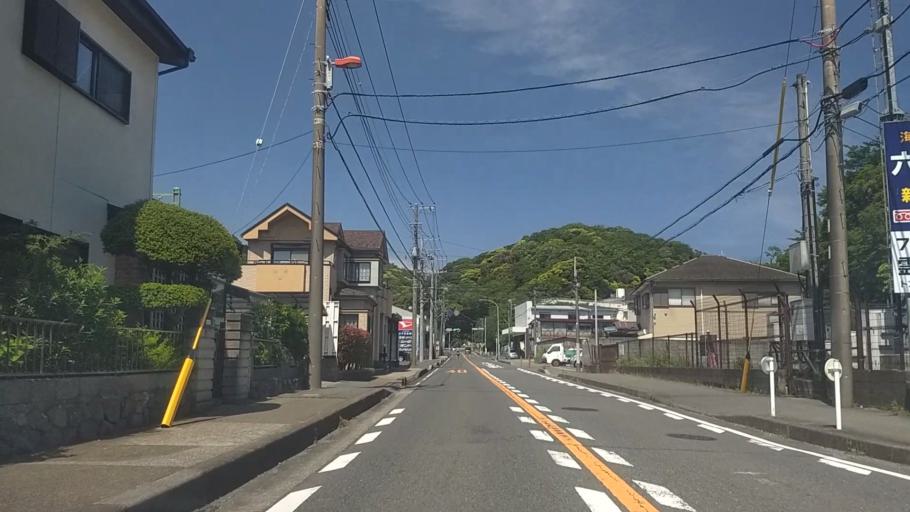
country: JP
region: Kanagawa
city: Zushi
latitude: 35.3098
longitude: 139.5989
